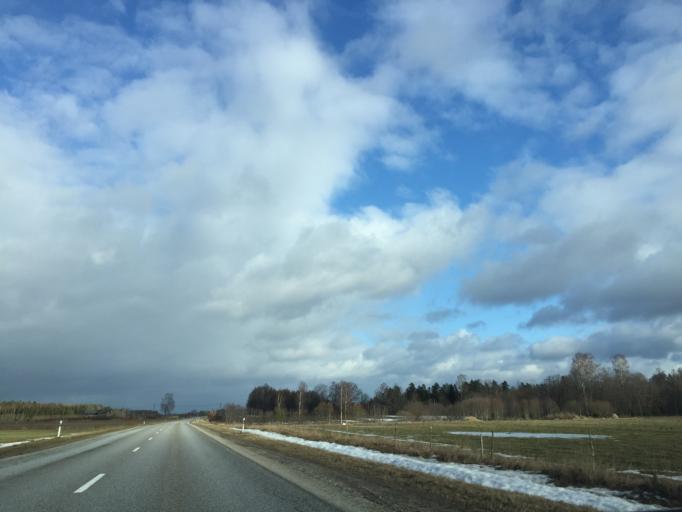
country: LV
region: Aloja
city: Staicele
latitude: 57.8748
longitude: 24.5803
